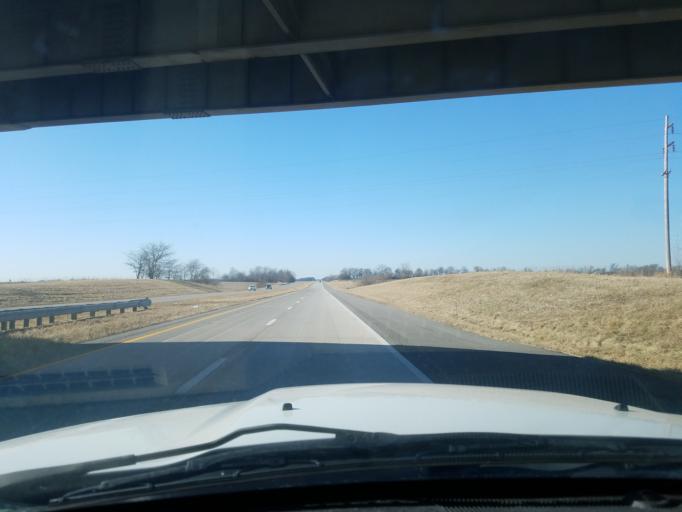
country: US
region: Kentucky
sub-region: Henderson County
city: Henderson
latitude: 37.7941
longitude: -87.4954
